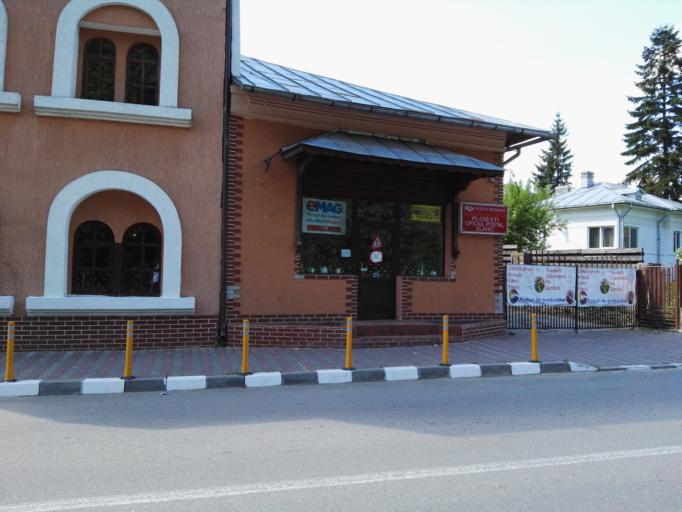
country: RO
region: Prahova
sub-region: Oras Slanic
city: Grosani
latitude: 45.2331
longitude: 25.9398
